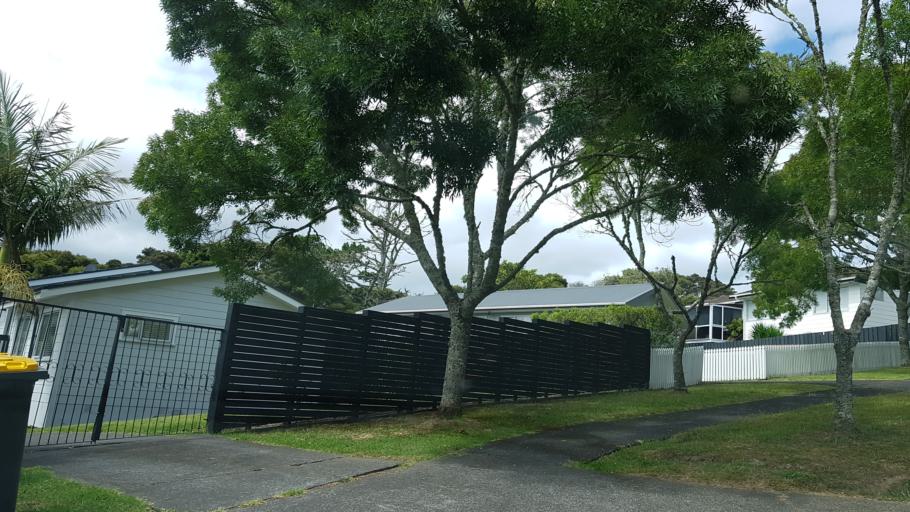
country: NZ
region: Auckland
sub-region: Auckland
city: North Shore
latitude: -36.7776
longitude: 174.7018
